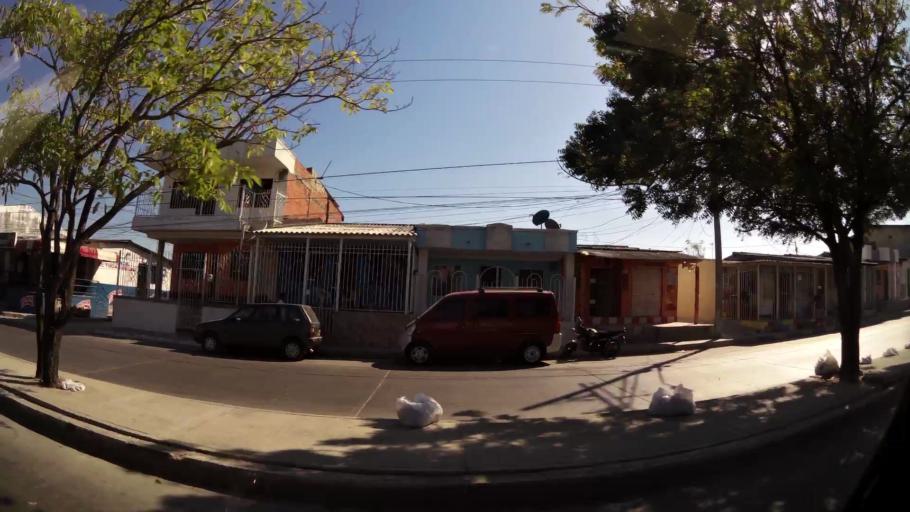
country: CO
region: Atlantico
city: Soledad
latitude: 10.9295
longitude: -74.7936
